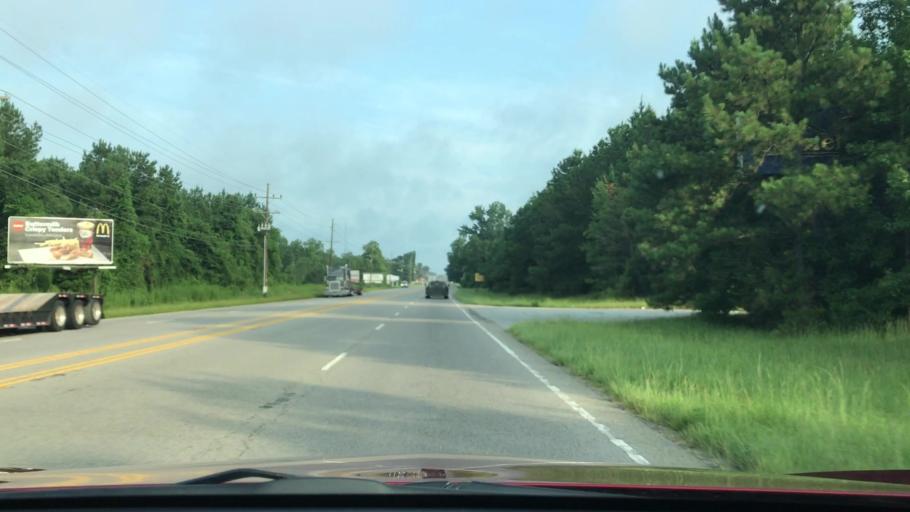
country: US
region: South Carolina
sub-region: Orangeburg County
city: Brookdale
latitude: 33.4729
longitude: -80.8085
